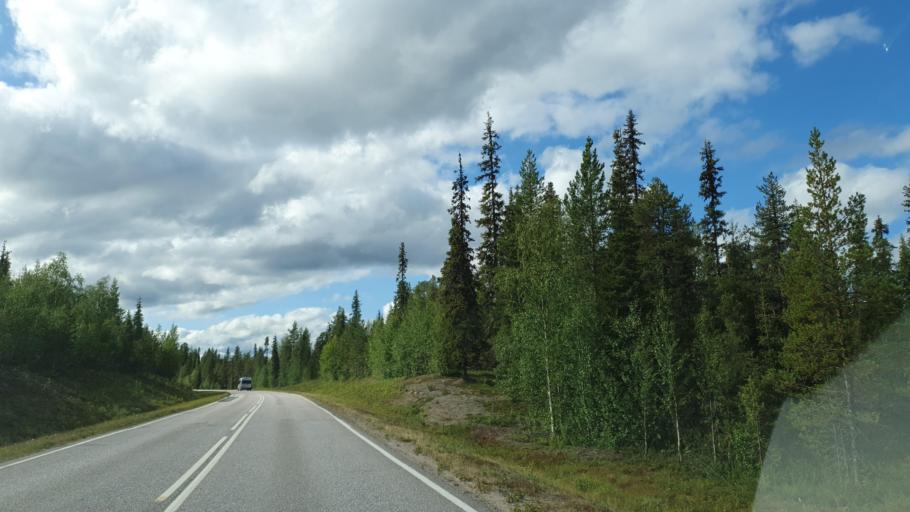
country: FI
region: Lapland
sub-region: Tunturi-Lappi
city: Muonio
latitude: 67.8712
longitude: 24.1830
